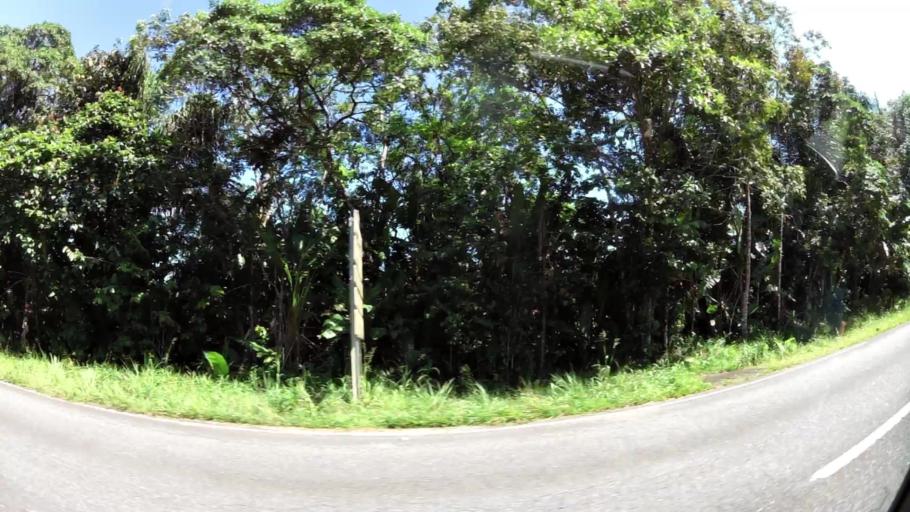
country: GF
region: Guyane
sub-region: Guyane
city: Matoury
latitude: 4.8315
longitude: -52.3509
